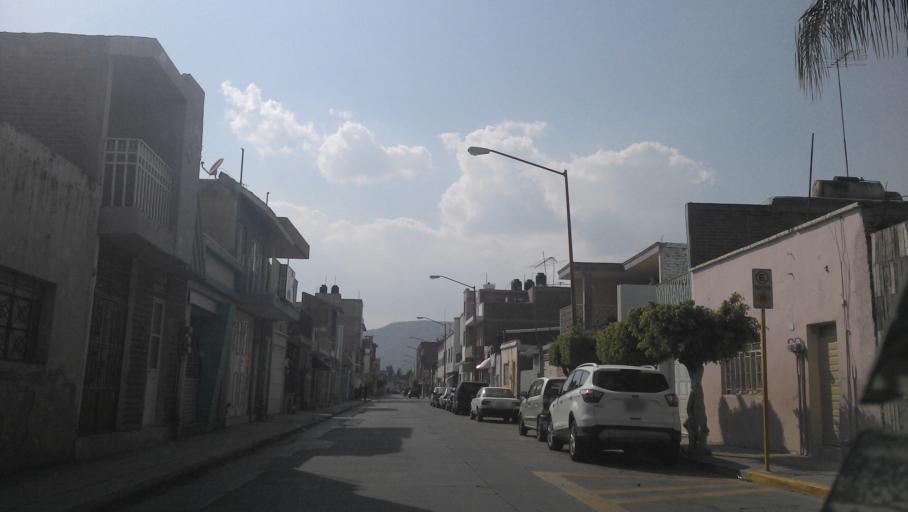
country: MX
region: Guanajuato
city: San Francisco del Rincon
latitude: 21.0218
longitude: -101.8569
